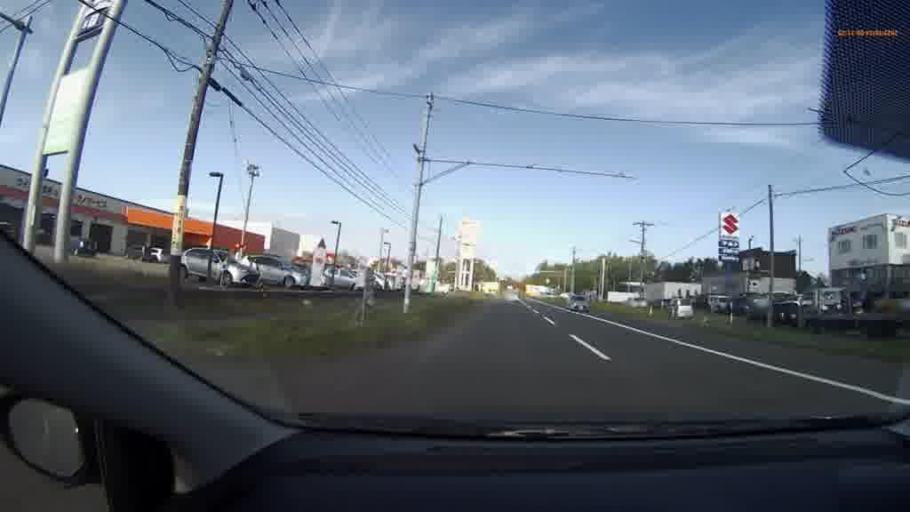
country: JP
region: Hokkaido
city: Kushiro
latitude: 43.0132
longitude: 144.4070
